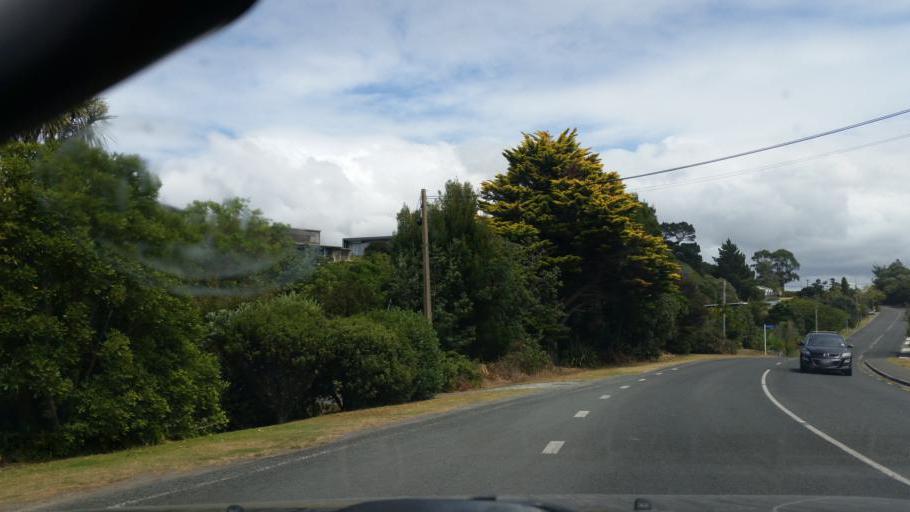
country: NZ
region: Auckland
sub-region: Auckland
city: Wellsford
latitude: -36.0864
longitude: 174.5867
